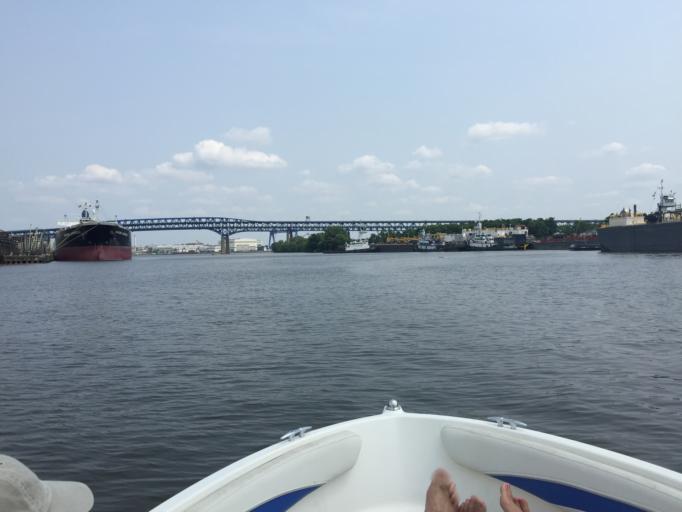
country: US
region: New Jersey
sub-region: Gloucester County
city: National Park
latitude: 39.8958
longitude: -75.2081
